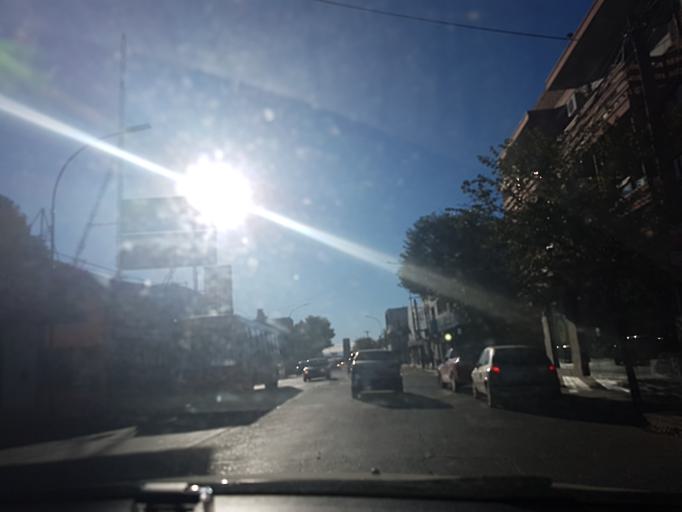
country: AR
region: Cordoba
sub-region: Departamento de Capital
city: Cordoba
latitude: -31.3975
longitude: -64.1992
